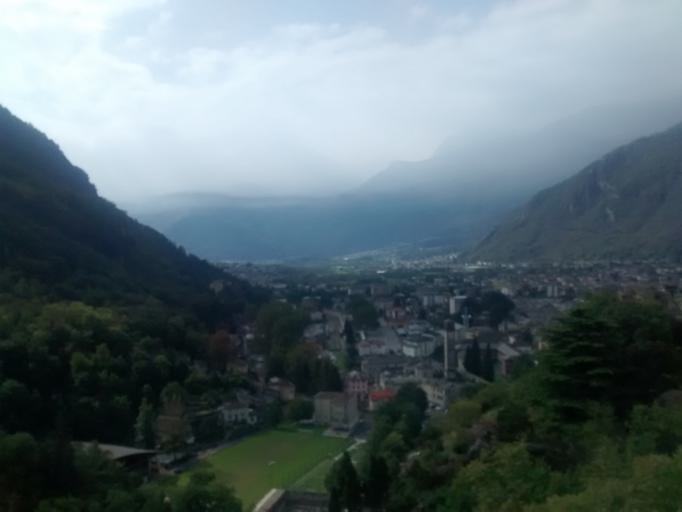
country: IT
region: Lombardy
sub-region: Provincia di Sondrio
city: Piuro
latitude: 46.3242
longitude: 9.4108
